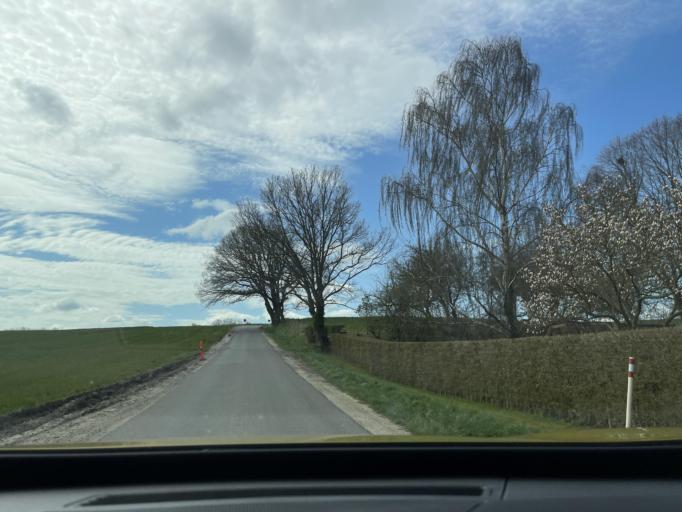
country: DK
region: Central Jutland
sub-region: Favrskov Kommune
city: Hinnerup
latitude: 56.2881
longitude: 10.0856
